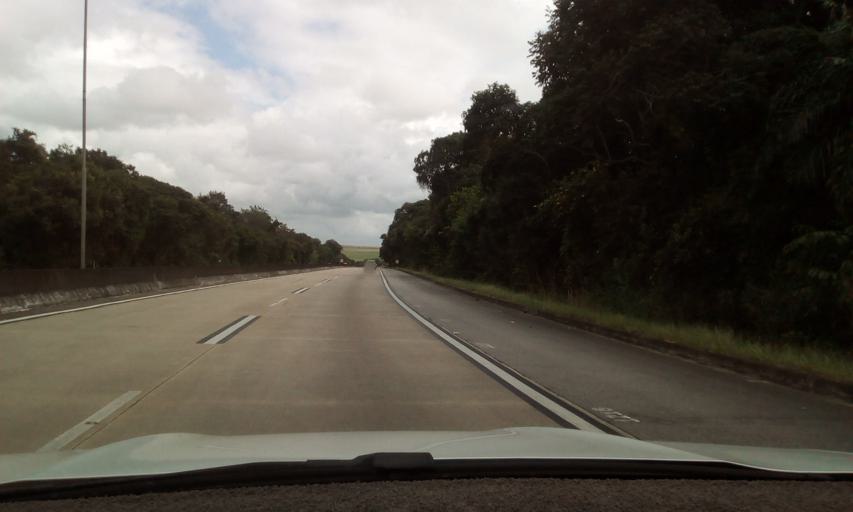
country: BR
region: Paraiba
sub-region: Santa Rita
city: Santa Rita
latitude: -7.0560
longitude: -35.0292
